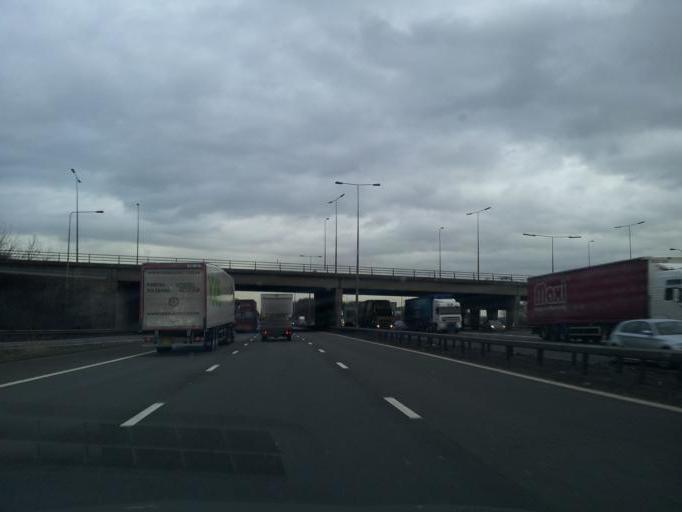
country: GB
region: England
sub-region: Warwickshire
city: Brandon
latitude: 52.4375
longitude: -1.4247
